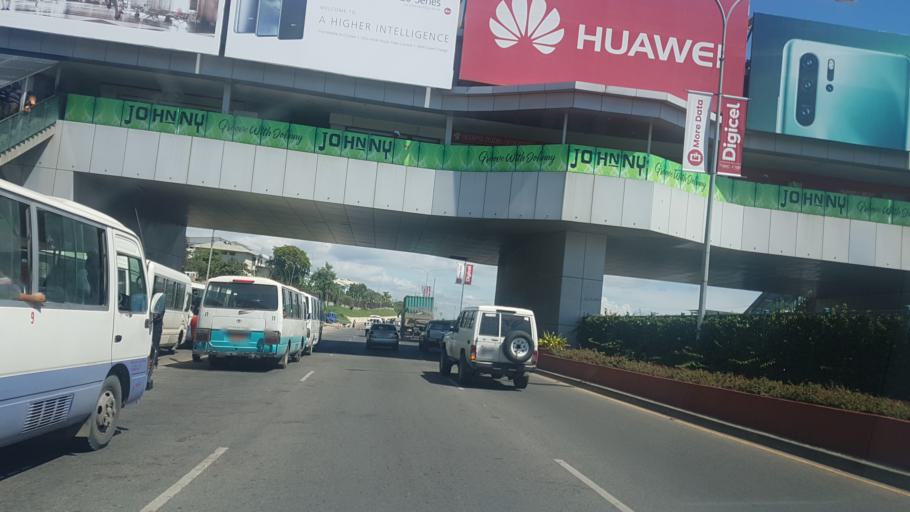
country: PG
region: National Capital
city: Port Moresby
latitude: -9.4389
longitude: 147.1803
